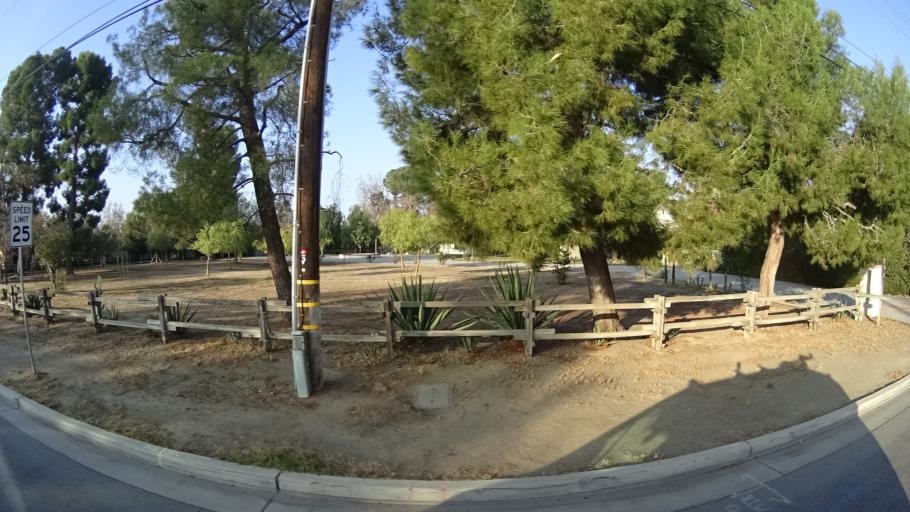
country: US
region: California
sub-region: Kern County
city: Bakersfield
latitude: 35.3606
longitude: -119.0459
